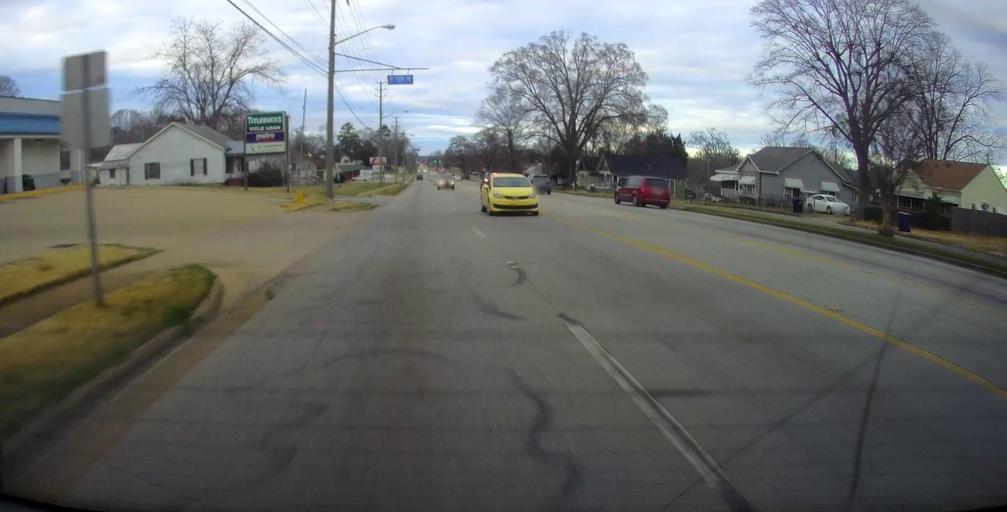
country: US
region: Alabama
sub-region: Chambers County
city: Lanett
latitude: 32.8570
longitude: -85.1917
